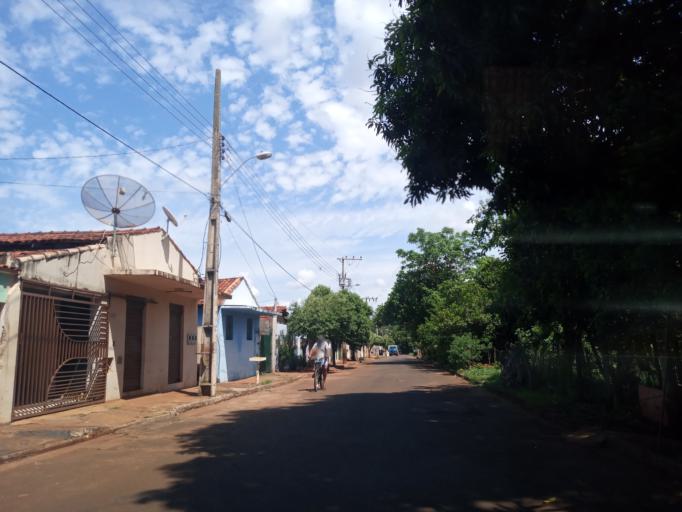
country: BR
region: Minas Gerais
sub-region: Ituiutaba
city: Ituiutaba
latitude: -18.9955
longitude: -49.4733
